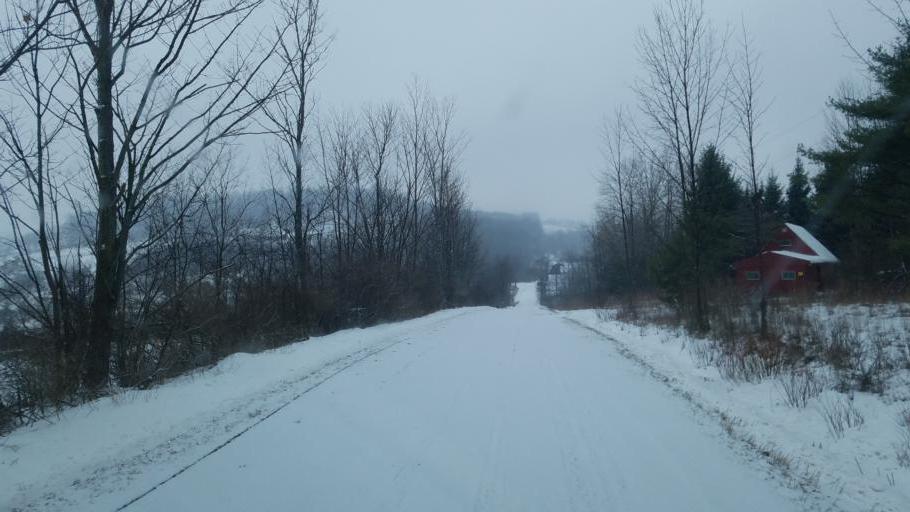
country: US
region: New York
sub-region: Steuben County
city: Canisteo
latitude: 42.1264
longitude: -77.5526
